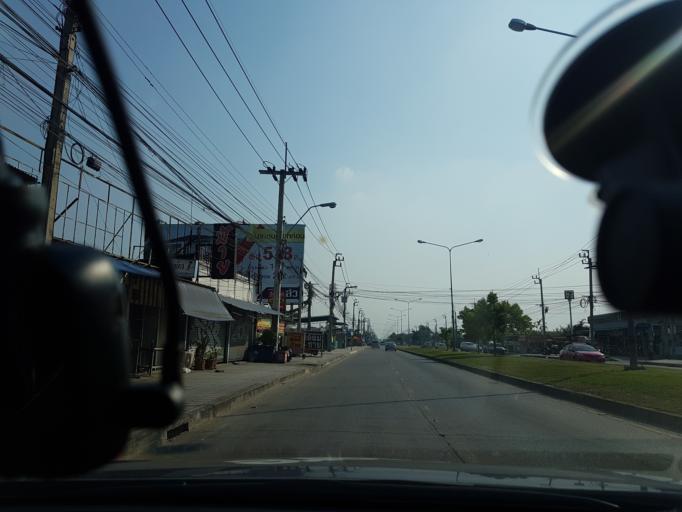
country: TH
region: Bangkok
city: Khlong Sam Wa
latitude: 13.8771
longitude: 100.7225
